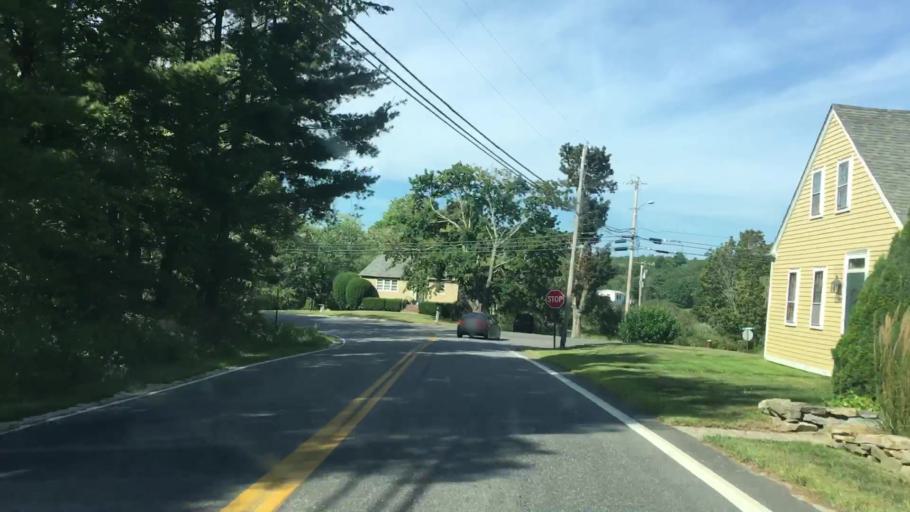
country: US
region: Maine
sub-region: Sagadahoc County
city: Bath
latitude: 43.9289
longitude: -69.8579
